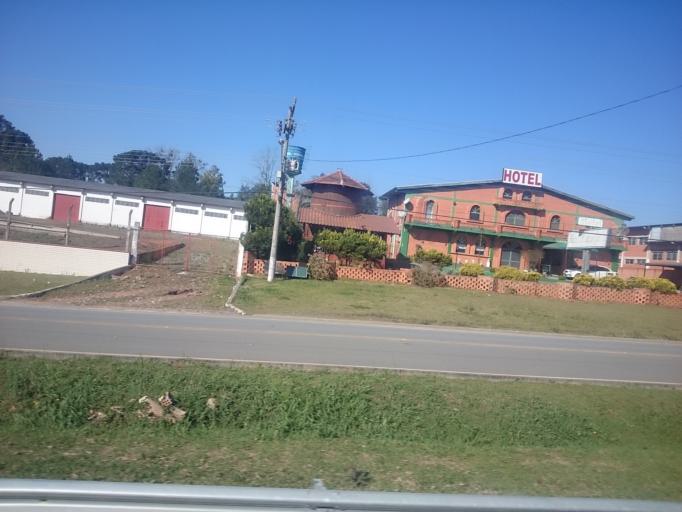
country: BR
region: Parana
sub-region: Rio Negro
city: Rio Negro
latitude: -26.0963
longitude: -49.7804
